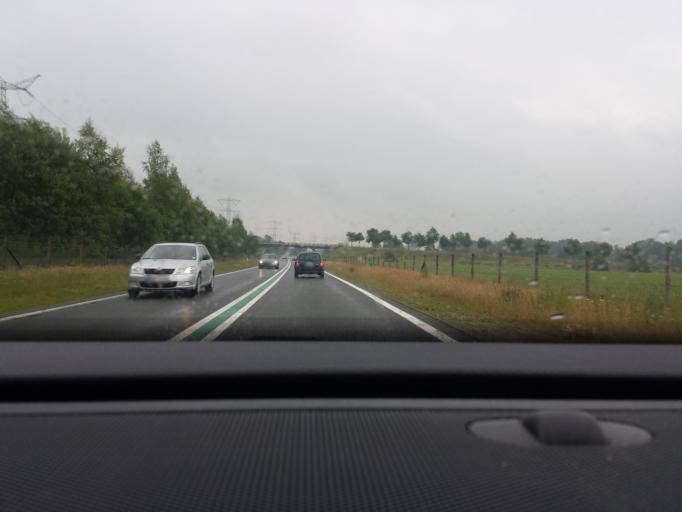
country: NL
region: Overijssel
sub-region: Gemeente Enschede
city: Enschede
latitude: 52.1966
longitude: 6.9457
